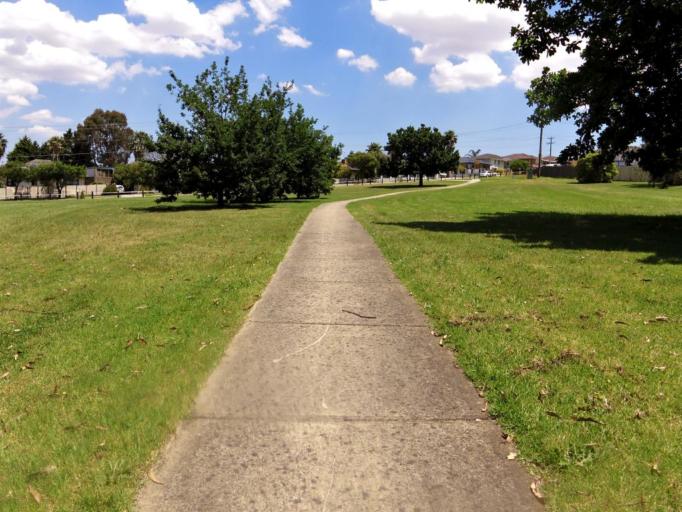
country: AU
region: Victoria
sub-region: Casey
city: Eumemmerring
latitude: -37.9879
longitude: 145.2501
